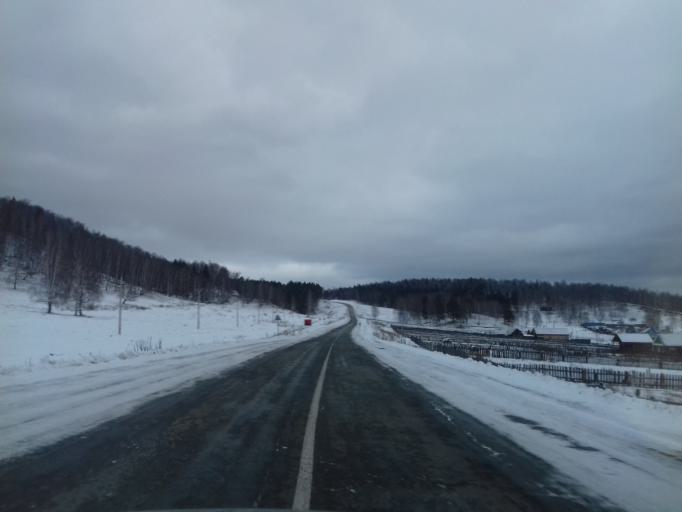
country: RU
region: Bashkortostan
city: Verkhniy Avzyan
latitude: 53.6439
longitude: 57.7859
